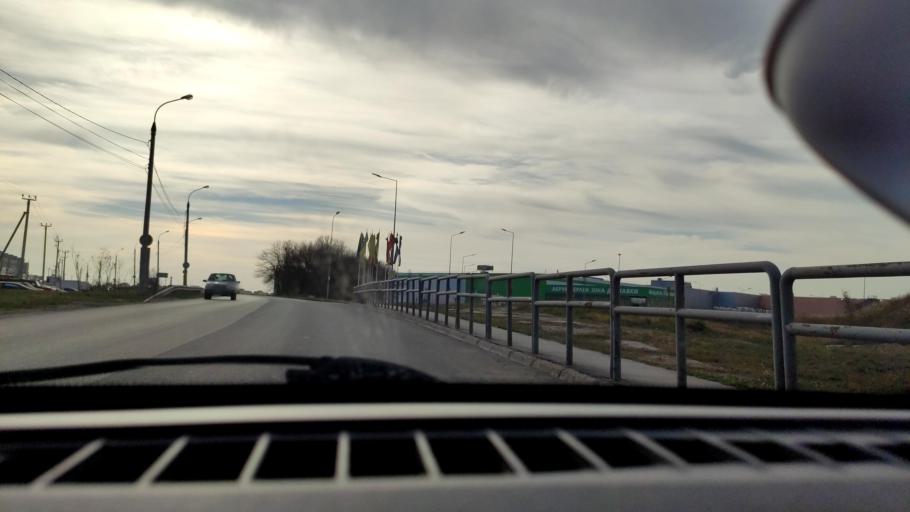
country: RU
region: Samara
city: Novosemeykino
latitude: 53.3285
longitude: 50.3120
